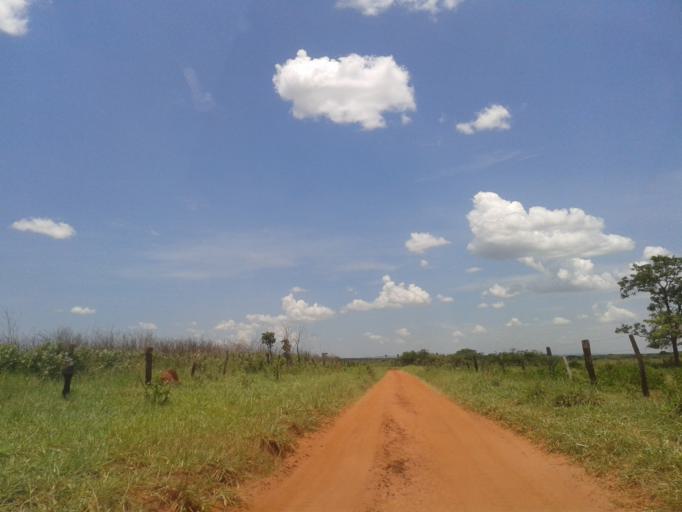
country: BR
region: Minas Gerais
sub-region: Santa Vitoria
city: Santa Vitoria
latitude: -19.2249
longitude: -50.4453
